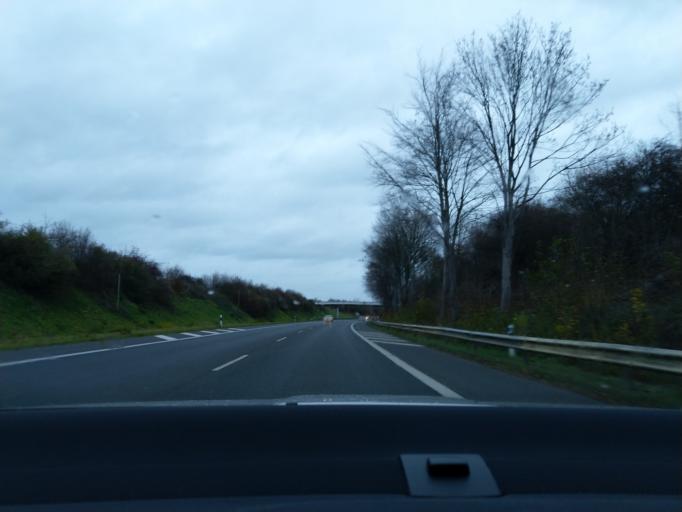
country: DE
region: North Rhine-Westphalia
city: Erkelenz
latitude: 51.0809
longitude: 6.2992
